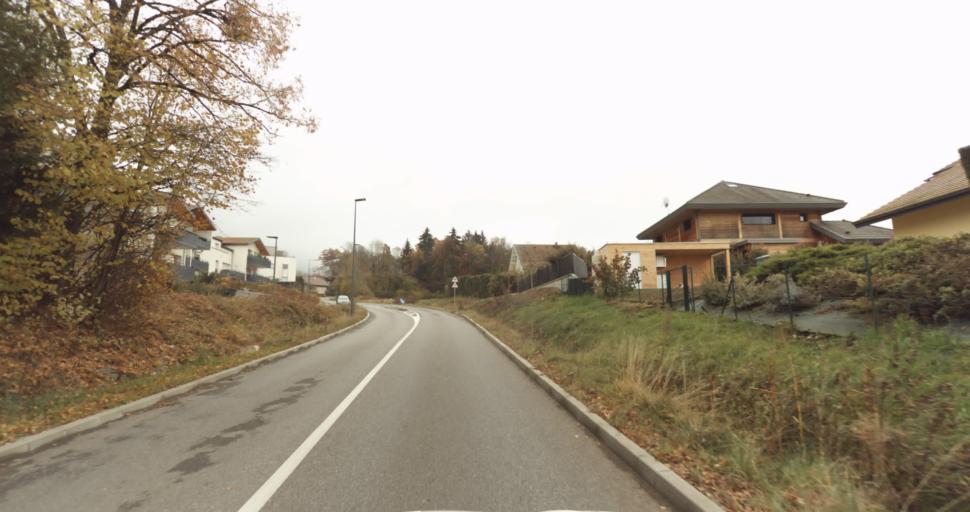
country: FR
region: Rhone-Alpes
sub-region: Departement de la Haute-Savoie
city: Seynod
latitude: 45.8568
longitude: 6.0891
